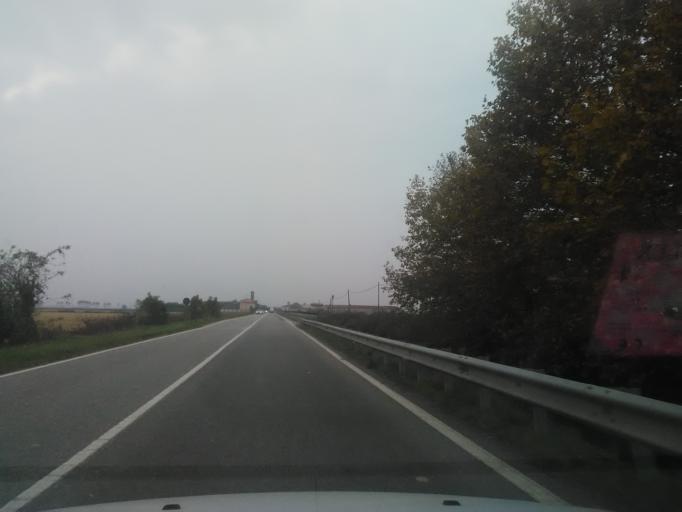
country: IT
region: Piedmont
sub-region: Provincia di Vercelli
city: Sali Vercellese
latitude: 45.3250
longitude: 8.3452
